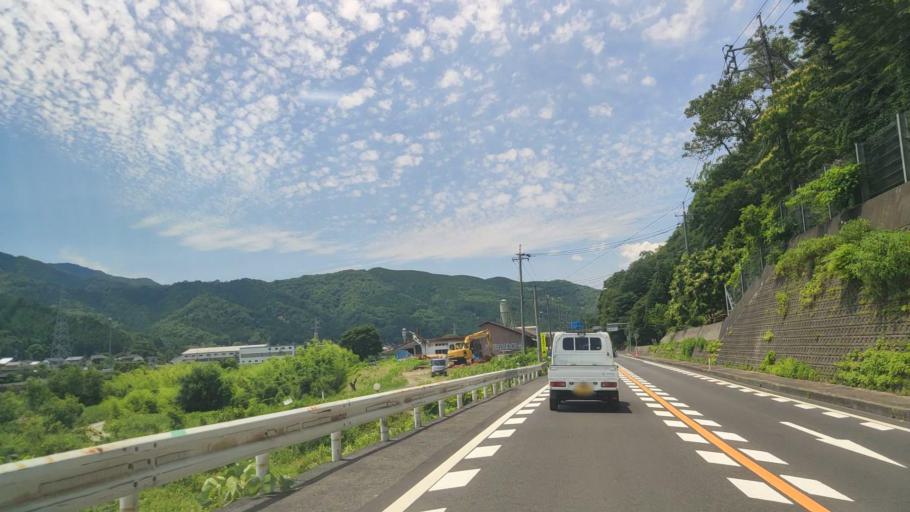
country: JP
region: Tottori
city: Tottori
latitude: 35.3664
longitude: 134.3242
